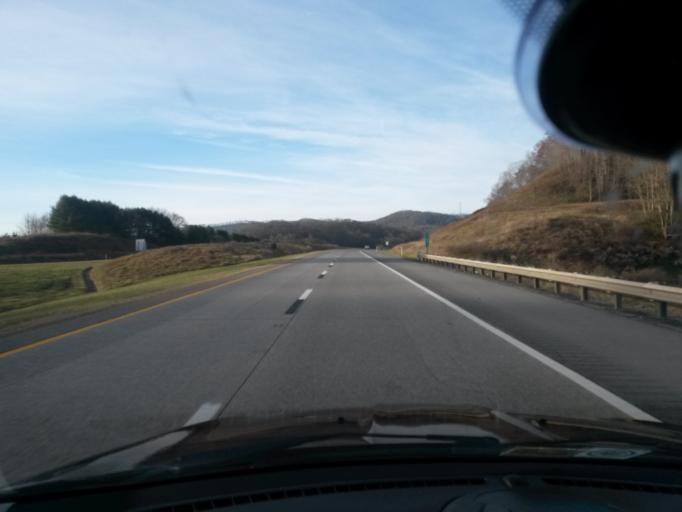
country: US
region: West Virginia
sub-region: Greenbrier County
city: Rainelle
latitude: 37.8469
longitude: -80.7290
